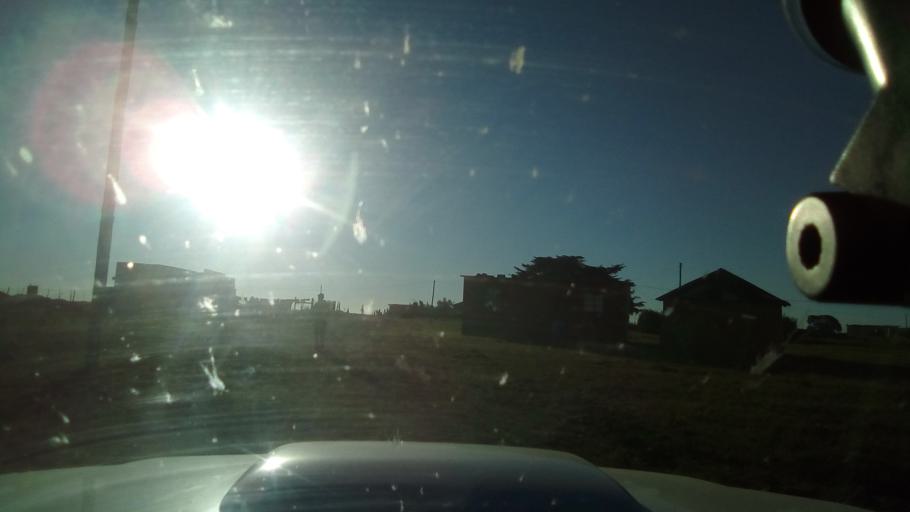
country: ZA
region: Eastern Cape
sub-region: Buffalo City Metropolitan Municipality
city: Bhisho
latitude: -32.9544
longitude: 27.3166
